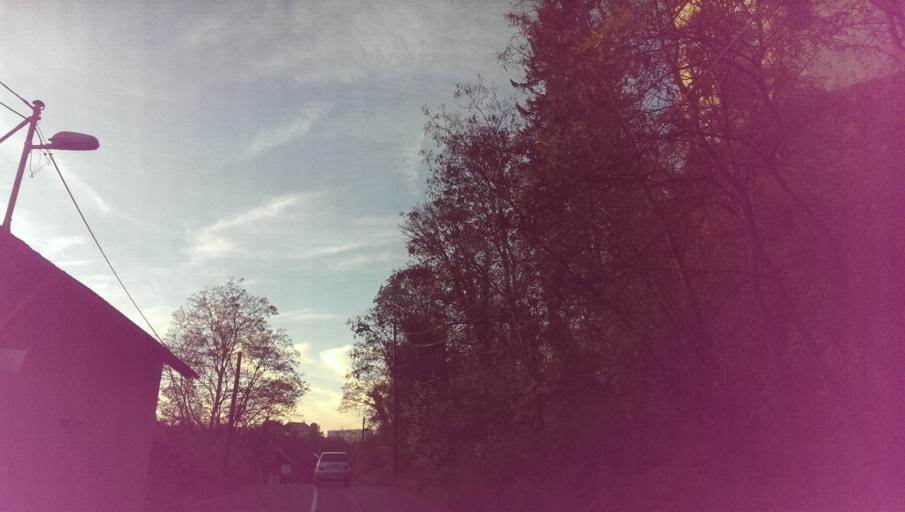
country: CZ
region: Zlin
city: Tecovice
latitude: 49.2030
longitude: 17.5998
